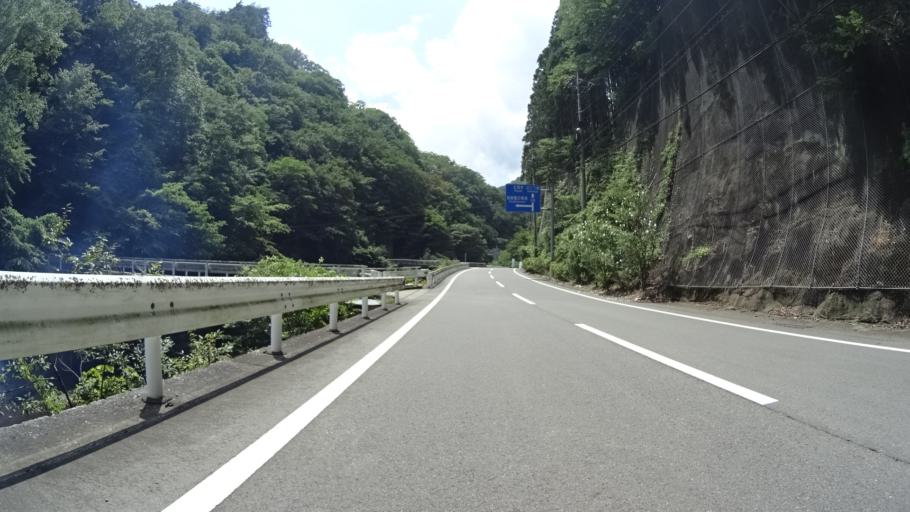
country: JP
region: Gunma
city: Tomioka
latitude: 36.0736
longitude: 138.7065
